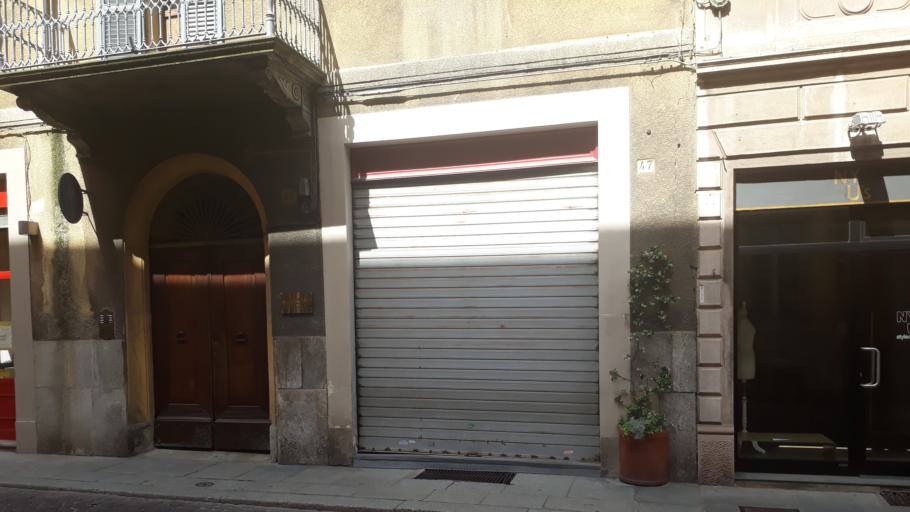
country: IT
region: Emilia-Romagna
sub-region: Provincia di Piacenza
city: Piacenza
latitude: 45.0522
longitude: 9.6912
